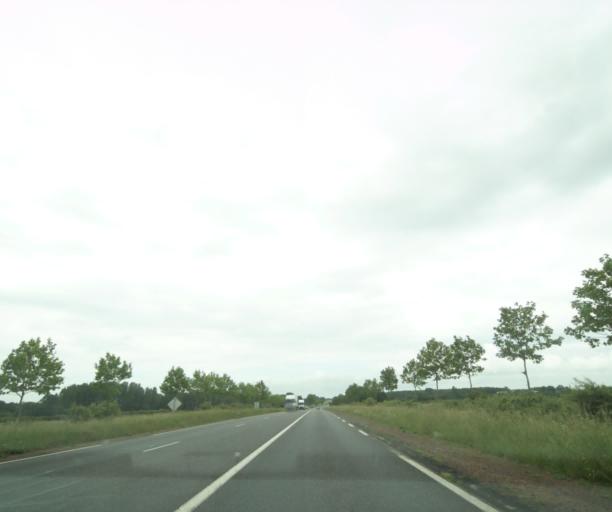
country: FR
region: Poitou-Charentes
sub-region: Departement des Deux-Sevres
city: Saint-Varent
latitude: 46.8437
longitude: -0.2085
